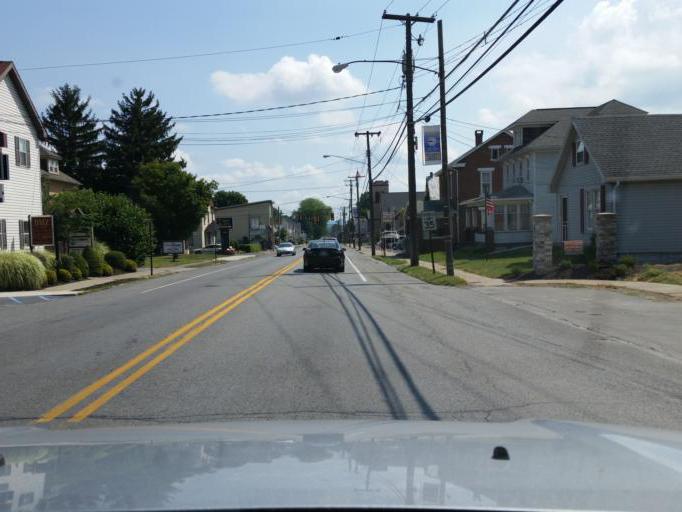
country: US
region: Pennsylvania
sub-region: Blair County
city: Duncansville
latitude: 40.4227
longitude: -78.4358
